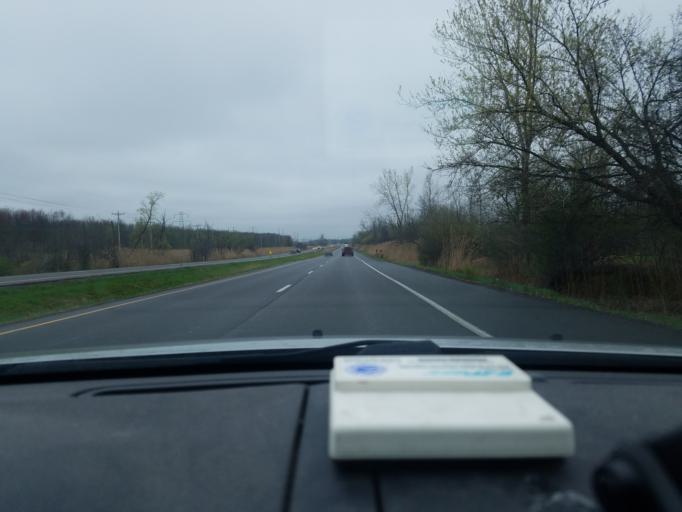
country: US
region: New York
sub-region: Onondaga County
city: East Syracuse
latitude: 43.1112
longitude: -76.0773
